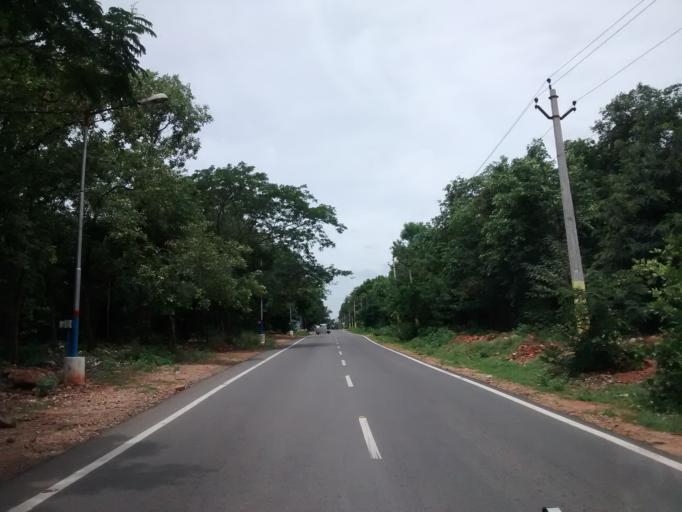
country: IN
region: Andhra Pradesh
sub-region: Chittoor
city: Akkarampalle
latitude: 13.6441
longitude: 79.4010
